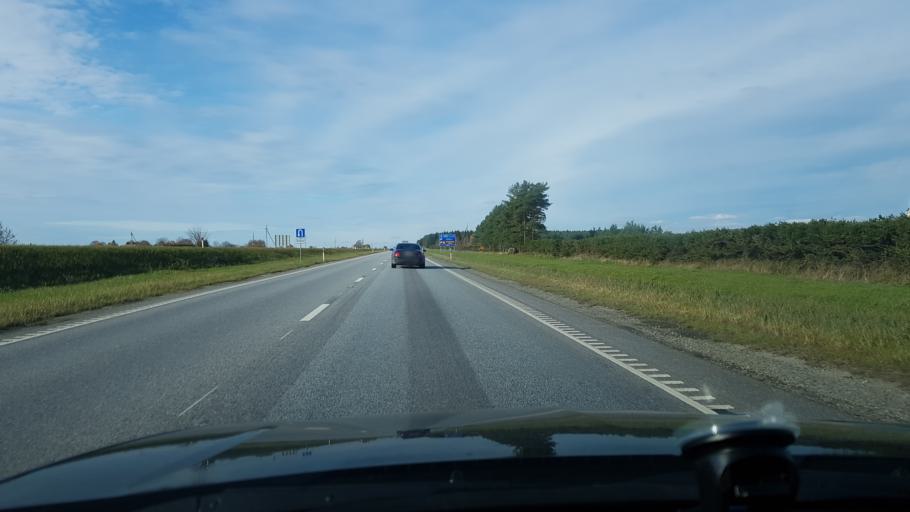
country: EE
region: Harju
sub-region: Raasiku vald
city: Raasiku
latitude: 59.4414
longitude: 25.1302
